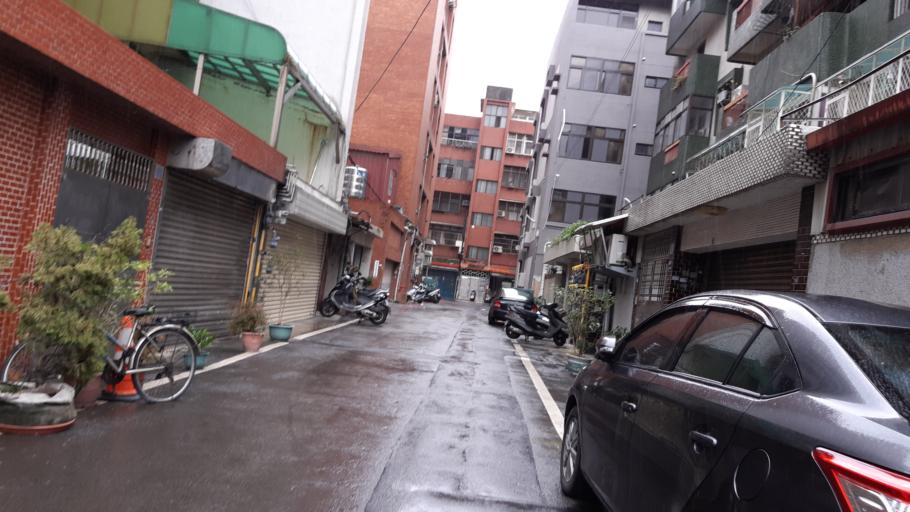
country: TW
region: Taiwan
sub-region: Hsinchu
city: Hsinchu
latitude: 24.8003
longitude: 120.9604
